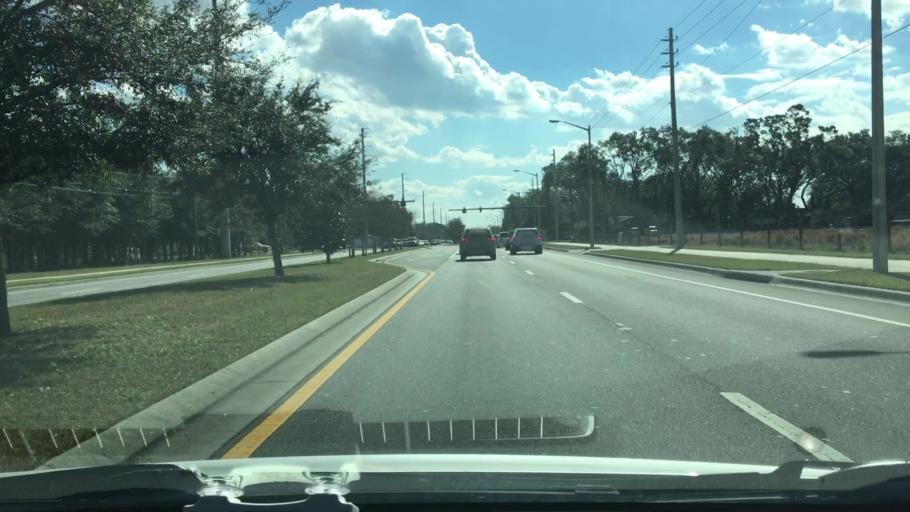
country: US
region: Florida
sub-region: Orange County
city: Conway
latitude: 28.4745
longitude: -81.3308
